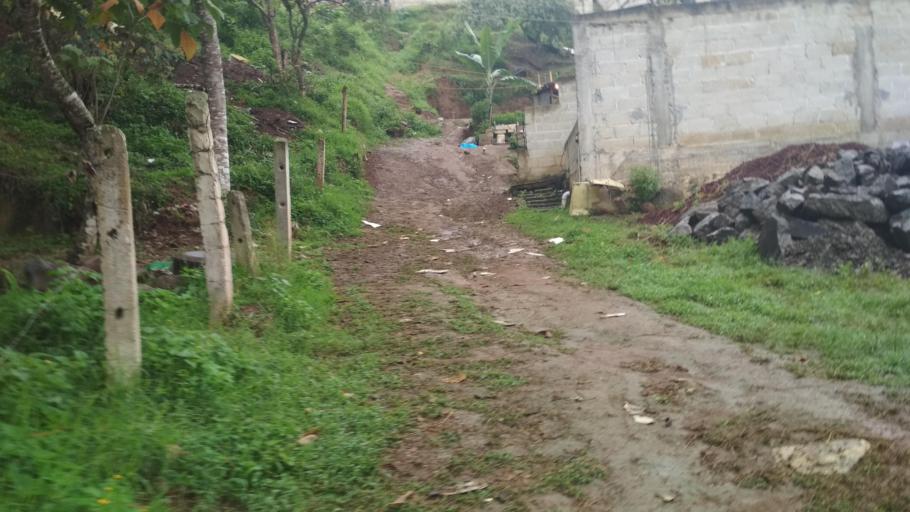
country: MX
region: Veracruz
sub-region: Emiliano Zapata
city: Las Trancas
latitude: 19.5062
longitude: -96.8679
